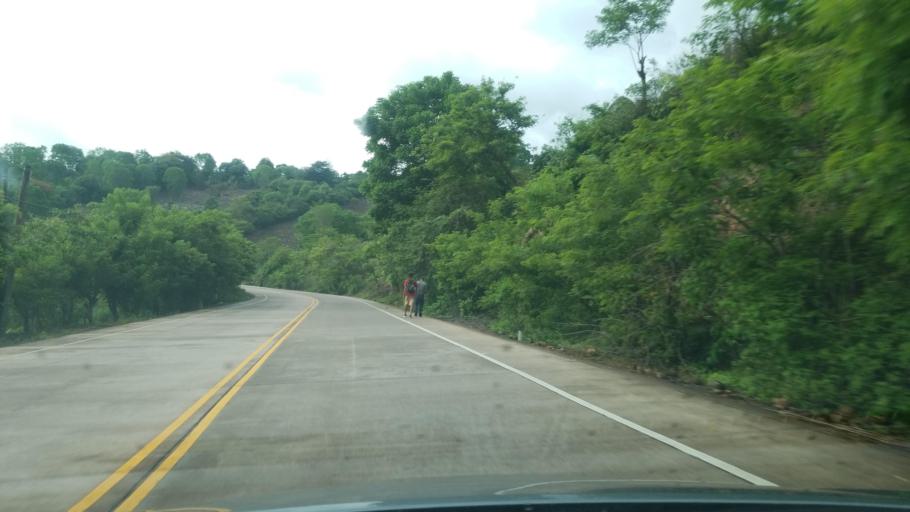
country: HN
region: Copan
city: Copan
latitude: 14.8401
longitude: -89.1860
